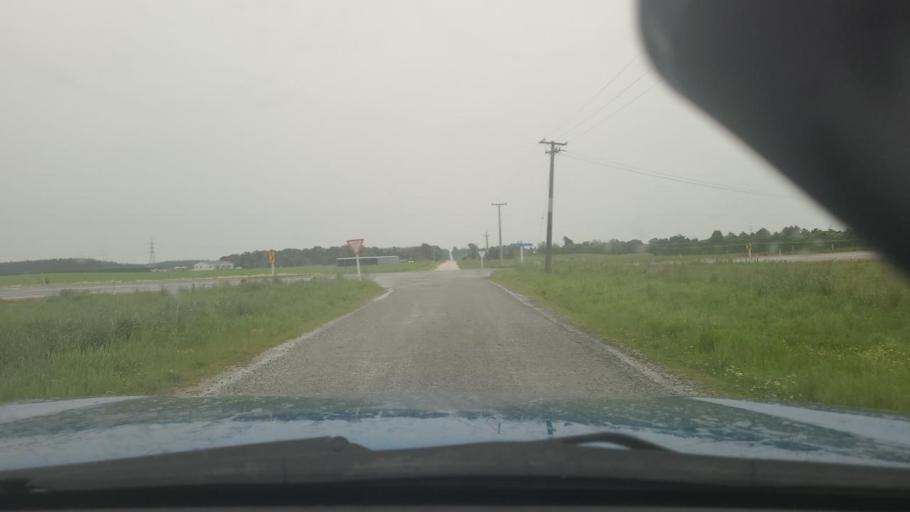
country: NZ
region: Southland
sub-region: Invercargill City
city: Invercargill
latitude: -46.4284
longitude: 168.4553
